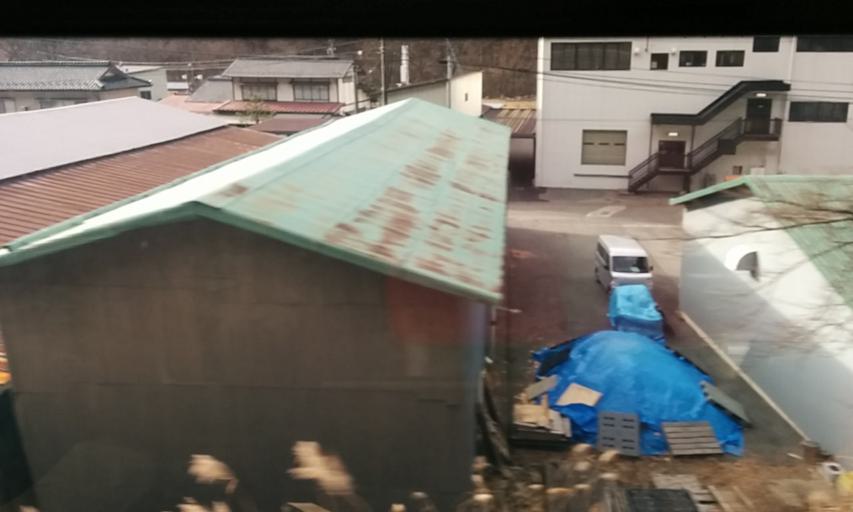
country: JP
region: Nagano
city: Tatsuno
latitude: 35.9931
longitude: 137.8522
